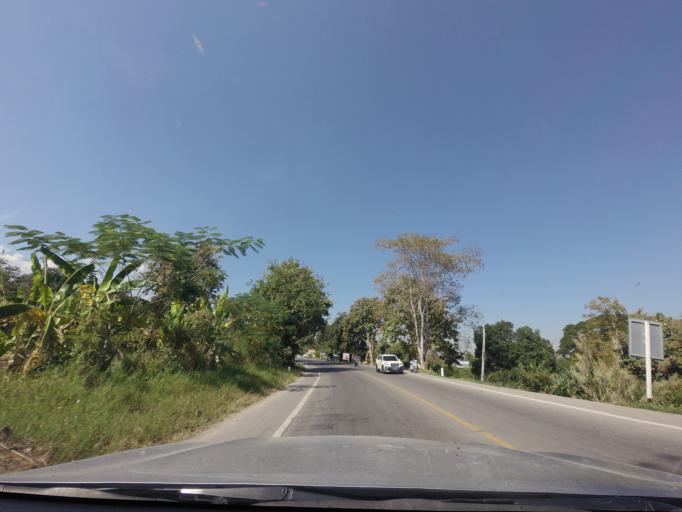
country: TH
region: Chiang Mai
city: San Sai
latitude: 18.9205
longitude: 98.9402
